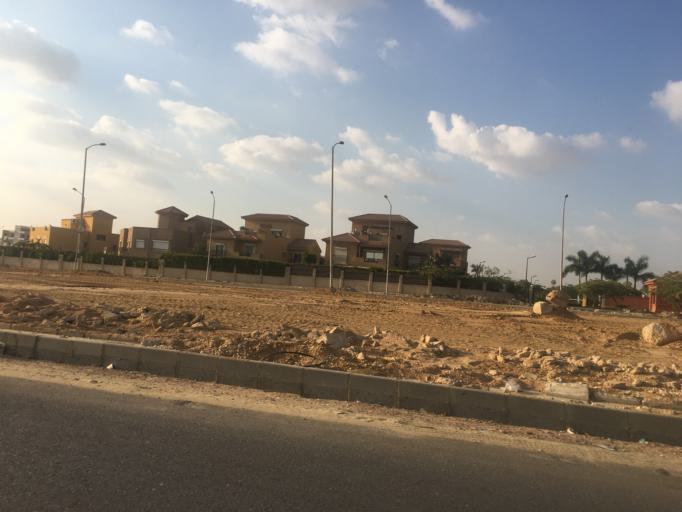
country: EG
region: Al Jizah
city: Madinat Sittah Uktubar
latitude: 29.9942
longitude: 30.9500
